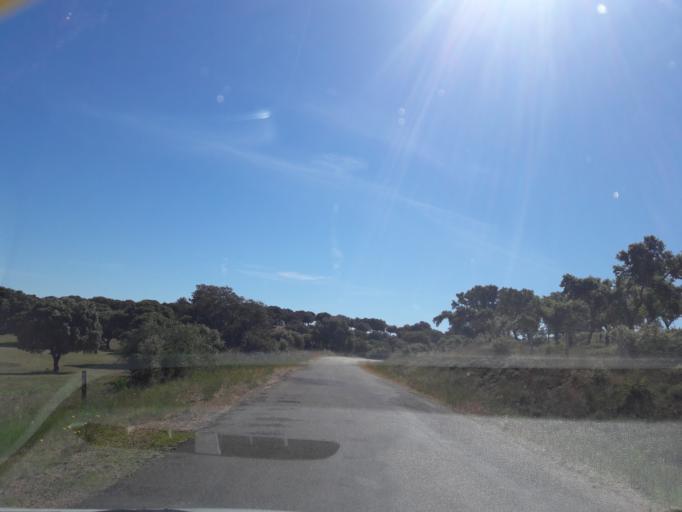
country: ES
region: Castille and Leon
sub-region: Provincia de Salamanca
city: Vega de Tirados
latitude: 41.0509
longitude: -5.8870
